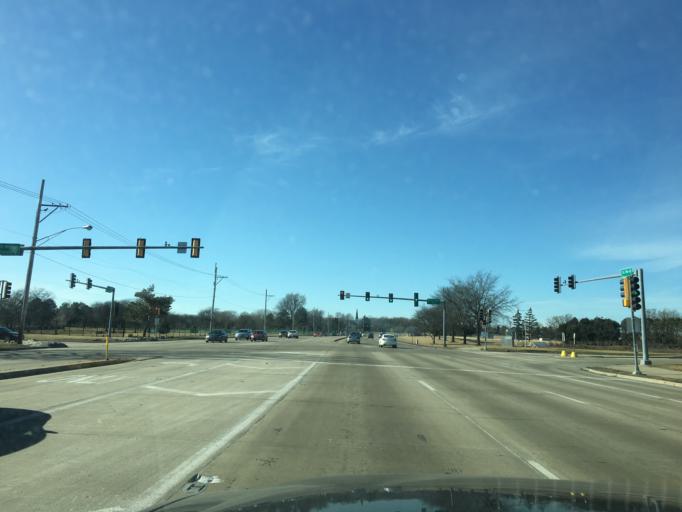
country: US
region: Illinois
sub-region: Cook County
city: Hoffman Estates
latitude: 42.0770
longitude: -88.0723
